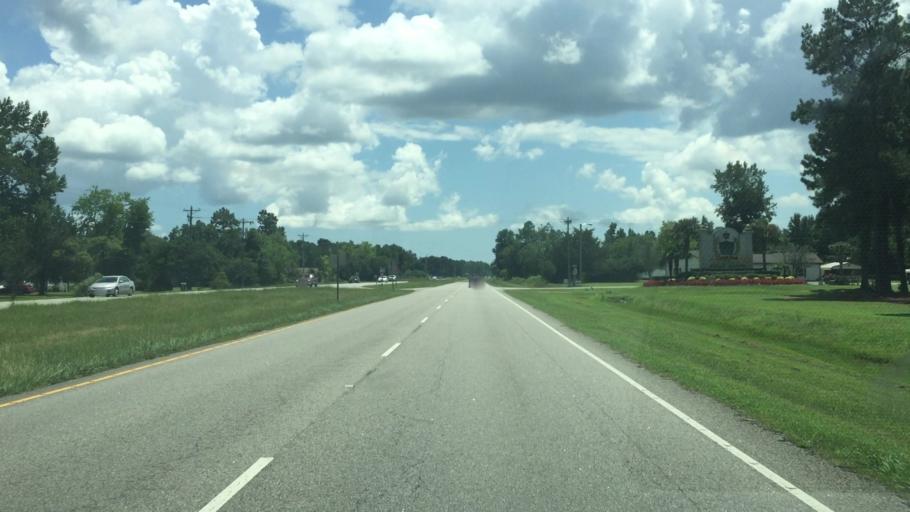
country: US
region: South Carolina
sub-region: Horry County
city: Loris
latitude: 33.9947
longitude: -78.7507
